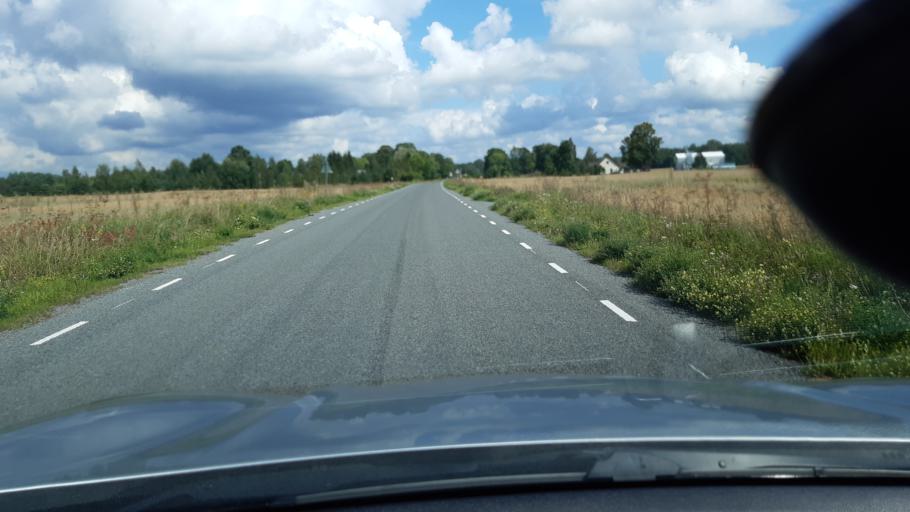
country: EE
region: Raplamaa
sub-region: Kehtna vald
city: Kehtna
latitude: 58.8737
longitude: 25.0053
